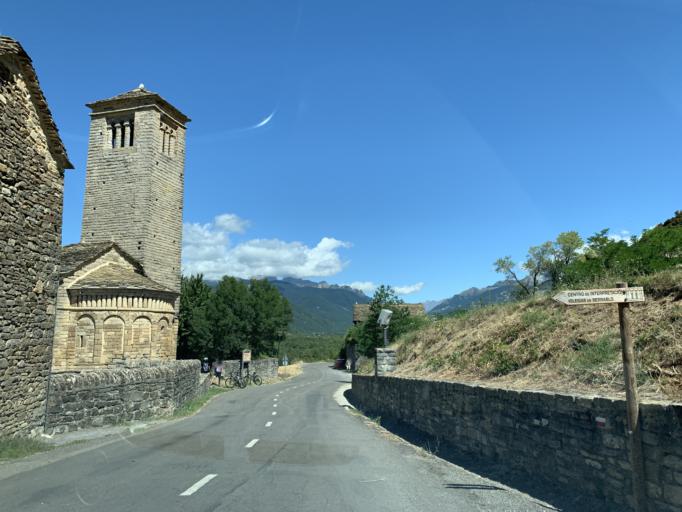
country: ES
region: Aragon
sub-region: Provincia de Huesca
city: Sabinanigo
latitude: 42.5541
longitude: -0.3177
